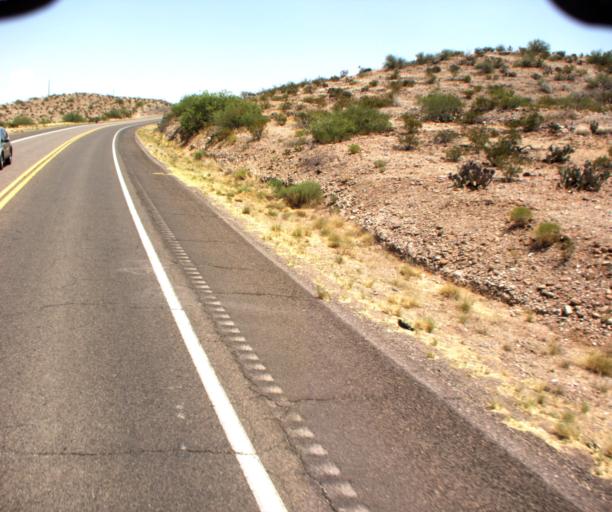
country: US
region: Arizona
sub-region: Graham County
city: Safford
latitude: 32.8128
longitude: -109.5936
